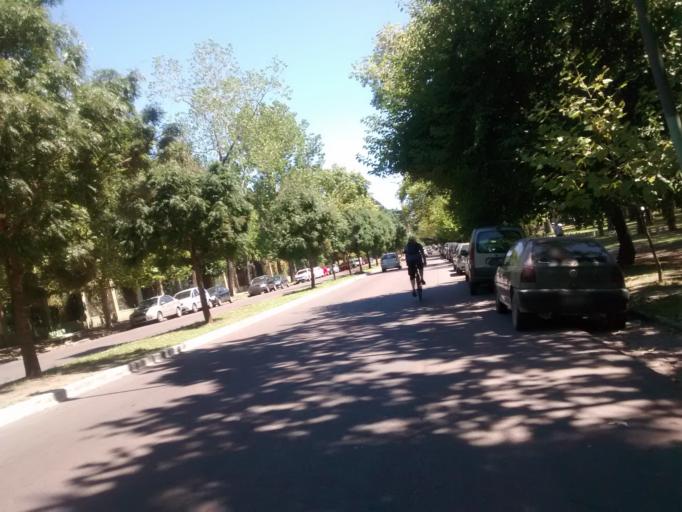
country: AR
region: Buenos Aires
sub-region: Partido de La Plata
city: La Plata
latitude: -34.9084
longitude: -57.9403
